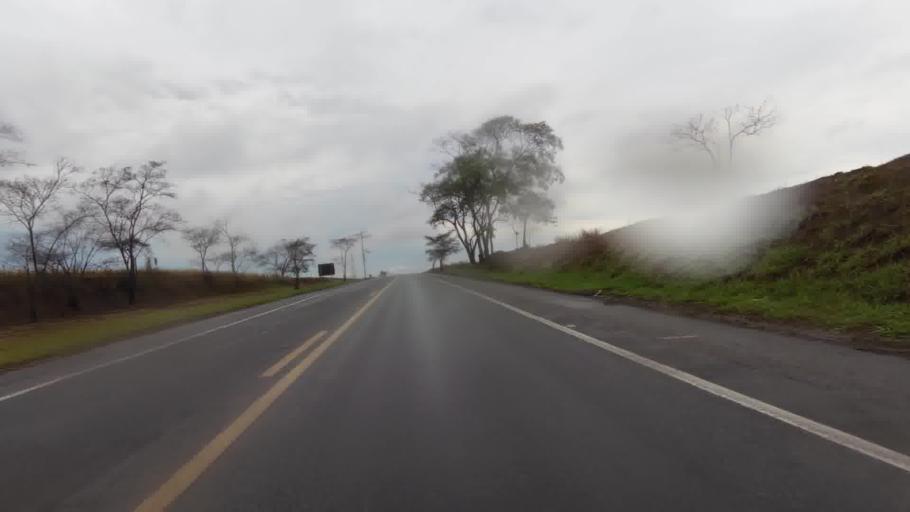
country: BR
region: Rio de Janeiro
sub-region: Campos Dos Goytacazes
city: Campos
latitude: -21.5252
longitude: -41.3368
